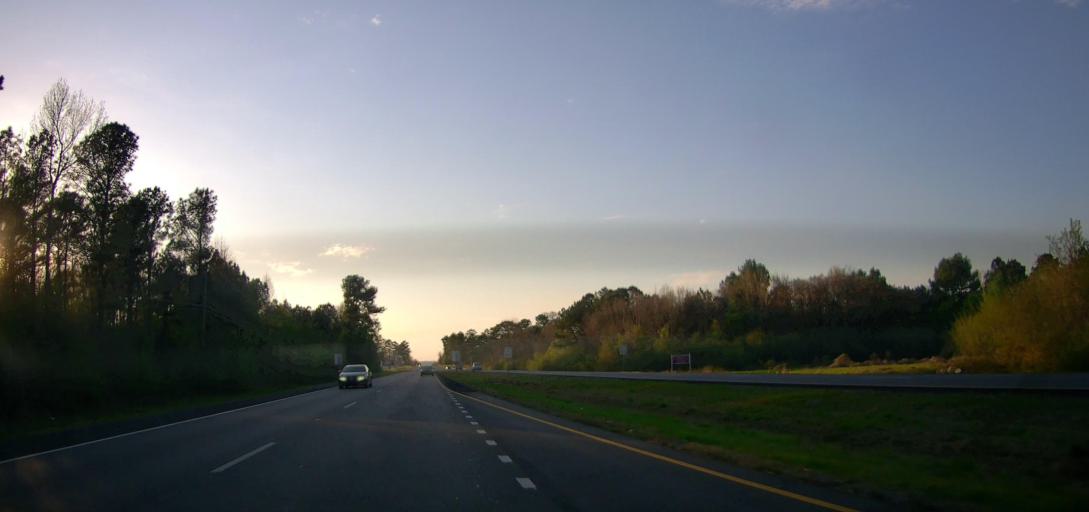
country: US
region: Alabama
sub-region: Shelby County
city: Harpersville
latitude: 33.3320
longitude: -86.4183
